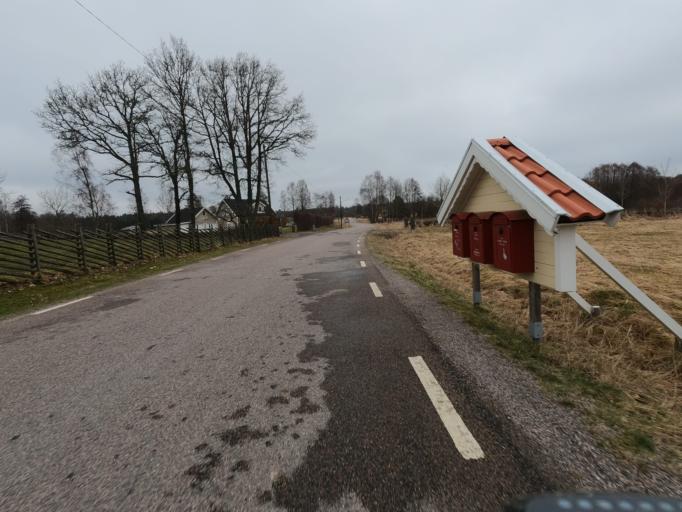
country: SE
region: Kronoberg
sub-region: Ljungby Kommun
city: Ljungby
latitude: 56.8309
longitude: 13.7602
